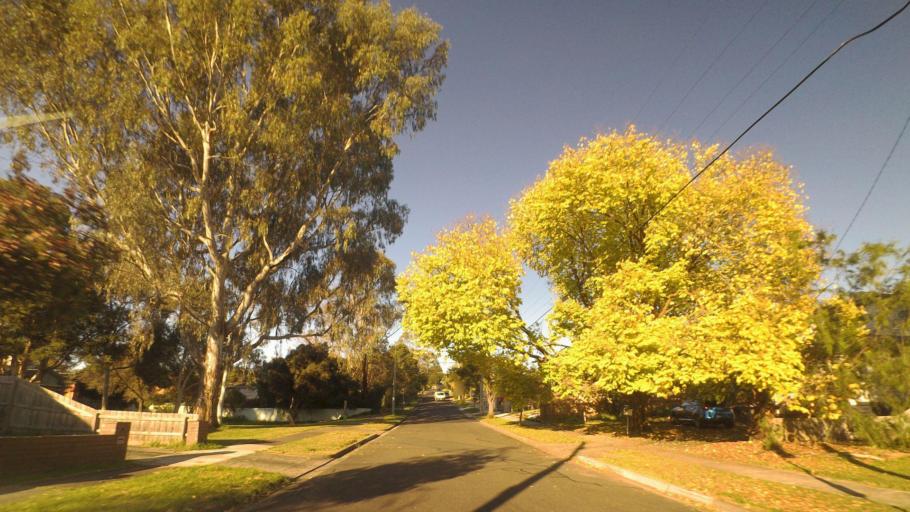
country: AU
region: Victoria
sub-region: Manningham
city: Doncaster East
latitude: -37.7971
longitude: 145.1532
